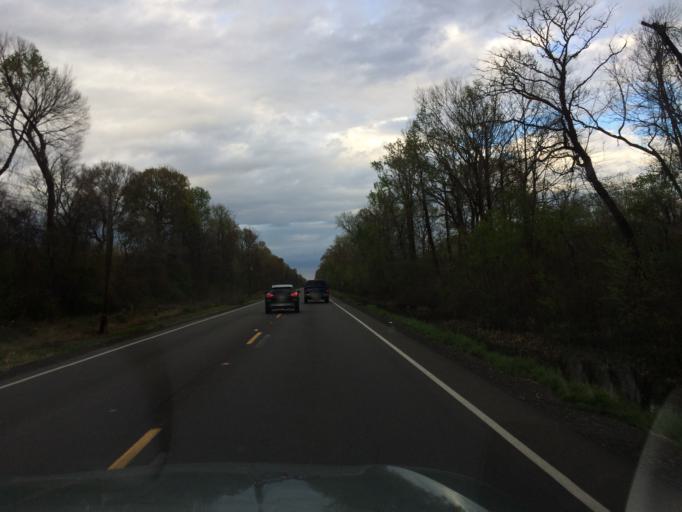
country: US
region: Louisiana
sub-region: West Baton Rouge Parish
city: Erwinville
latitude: 30.4646
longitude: -91.4126
